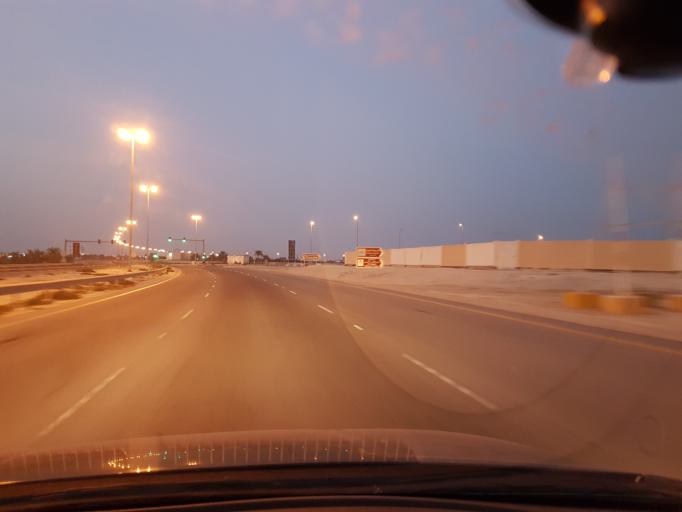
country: BH
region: Central Governorate
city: Dar Kulayb
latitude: 26.0174
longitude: 50.4882
